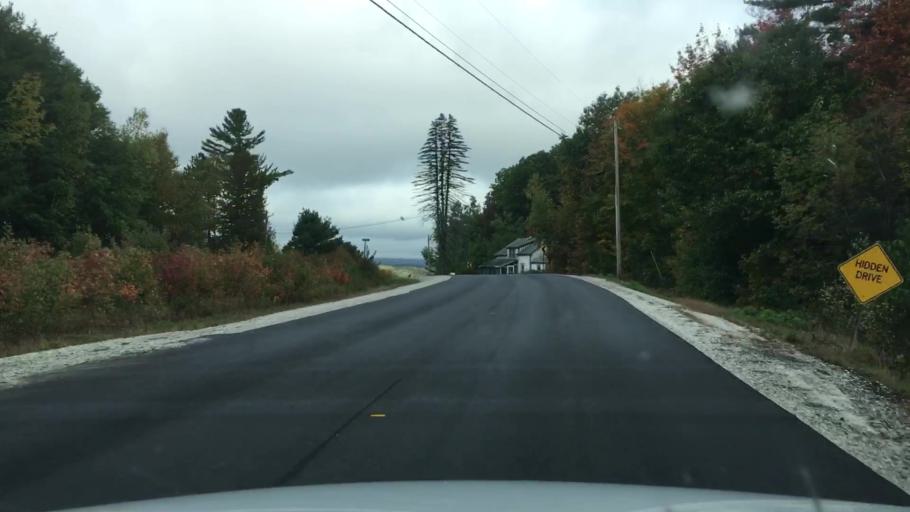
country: US
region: Maine
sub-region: Oxford County
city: Bethel
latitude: 44.3011
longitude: -70.7446
